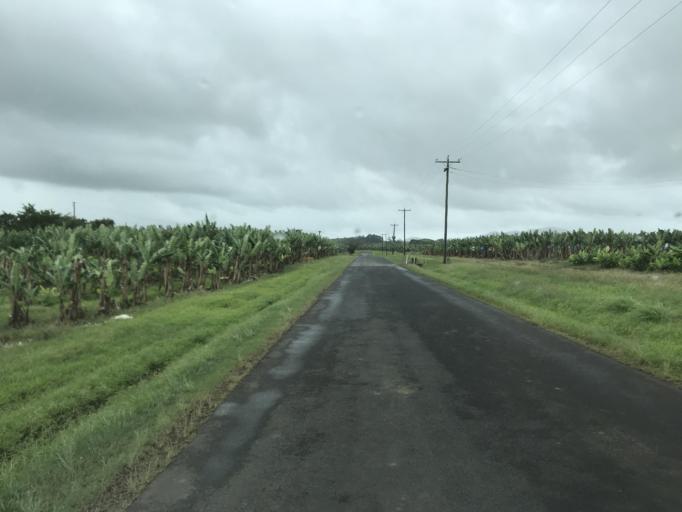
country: AU
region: Queensland
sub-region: Cassowary Coast
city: Innisfail
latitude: -17.5140
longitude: 145.9788
